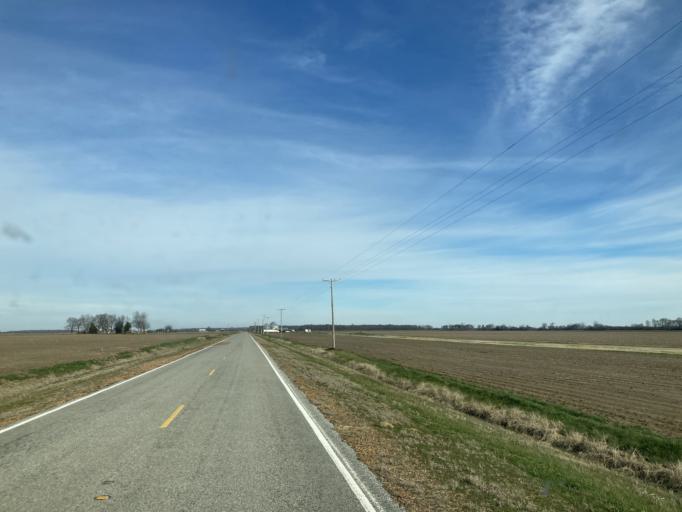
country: US
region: Mississippi
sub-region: Humphreys County
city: Belzoni
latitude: 33.0240
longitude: -90.6230
